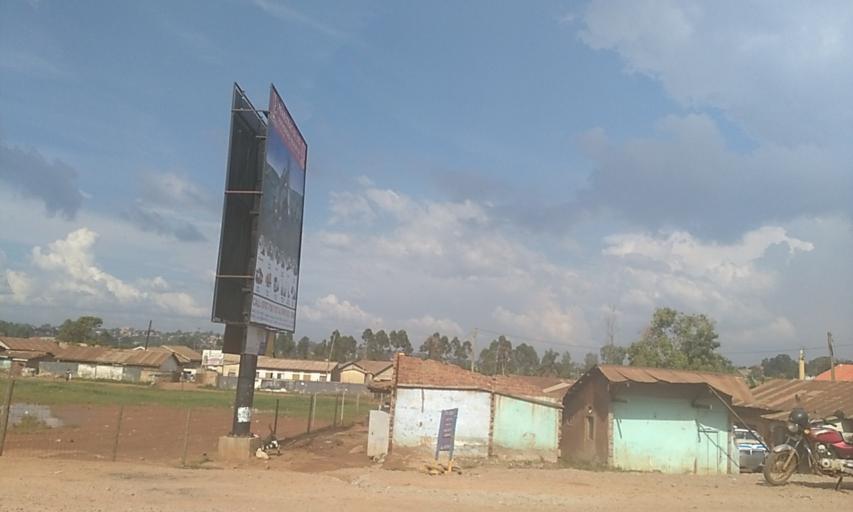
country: UG
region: Central Region
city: Kampala Central Division
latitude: 0.3438
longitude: 32.5435
